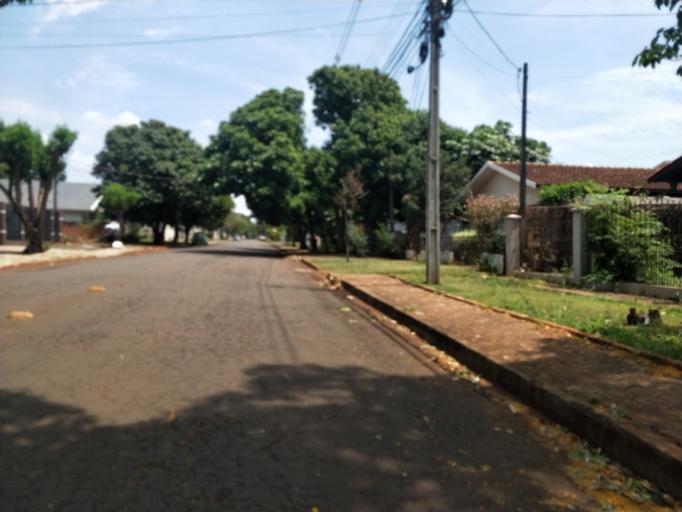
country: BR
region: Parana
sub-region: Marechal Candido Rondon
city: Marechal Candido Rondon
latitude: -24.5598
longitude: -54.0503
